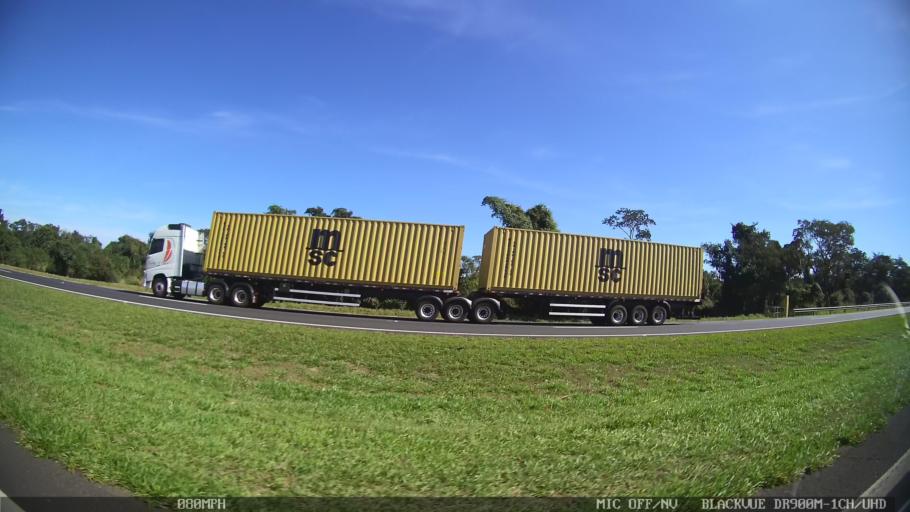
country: BR
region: Sao Paulo
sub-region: Santa Rita Do Passa Quatro
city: Santa Rita do Passa Quatro
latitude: -21.6319
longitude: -47.6134
